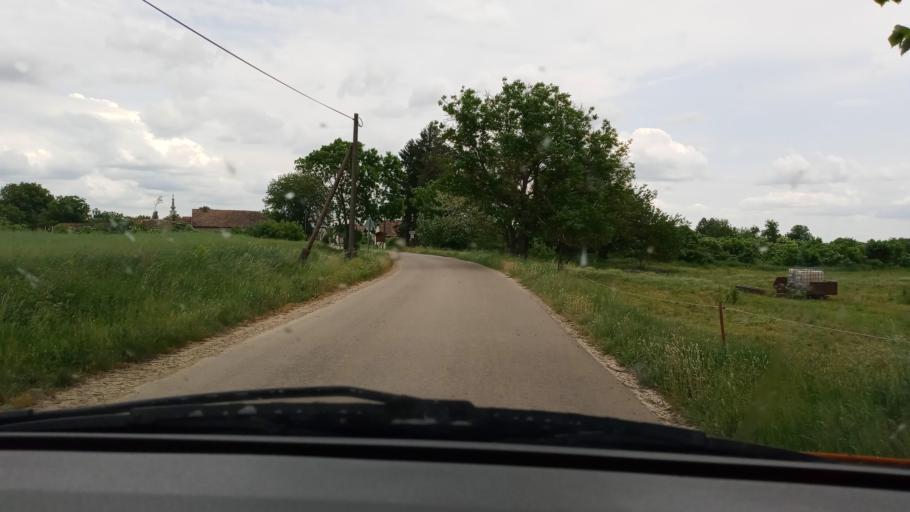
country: HU
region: Baranya
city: Vajszlo
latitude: 45.8272
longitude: 17.9871
